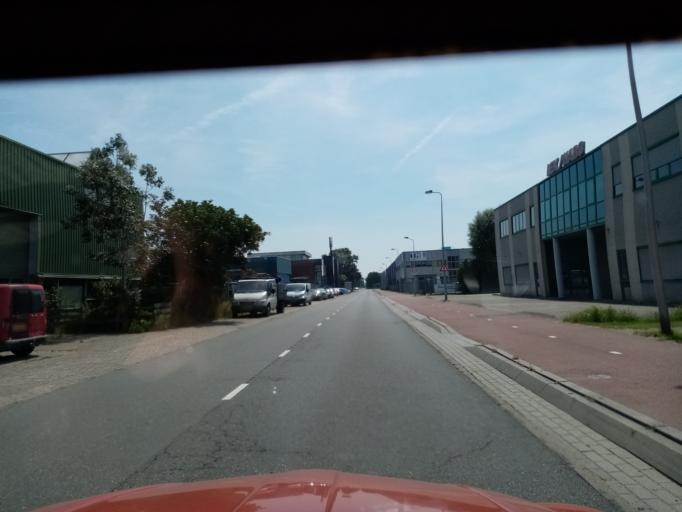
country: NL
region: South Holland
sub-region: Gemeente Kaag en Braassem
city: Leimuiden
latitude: 52.1790
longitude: 4.7129
